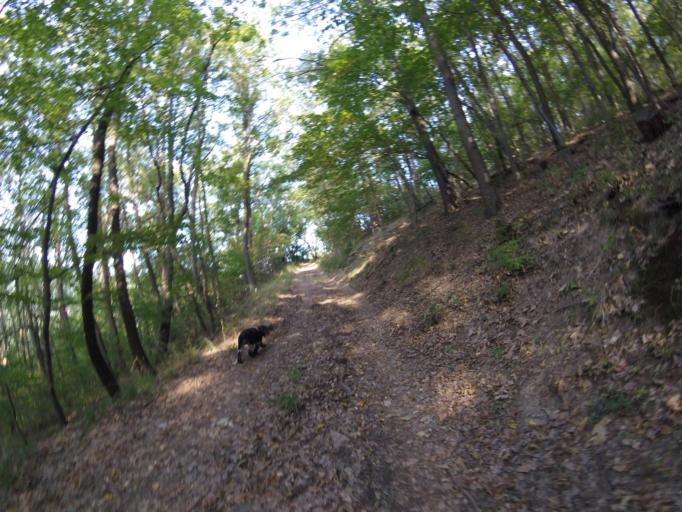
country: HU
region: Pest
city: Pilisszentkereszt
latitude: 47.7021
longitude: 18.9017
